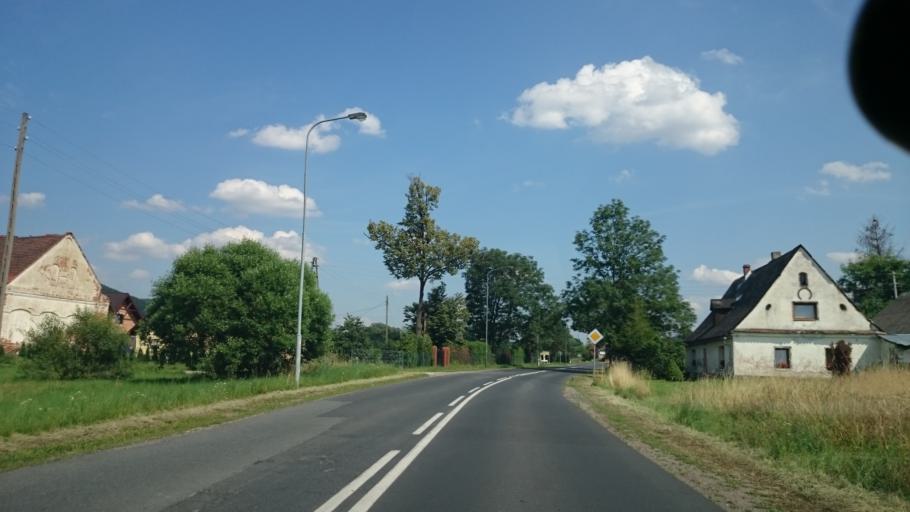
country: PL
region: Lower Silesian Voivodeship
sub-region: Powiat klodzki
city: Klodzko
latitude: 50.3679
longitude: 16.6848
